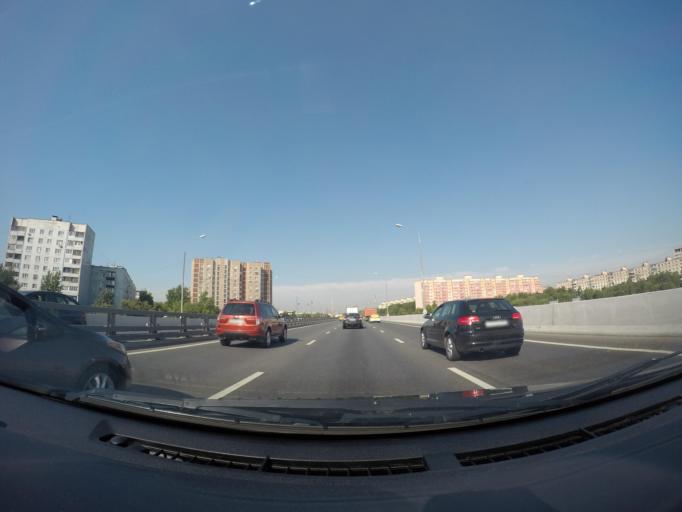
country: RU
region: Moscow
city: Tekstil'shchiki
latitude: 55.7081
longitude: 37.7464
